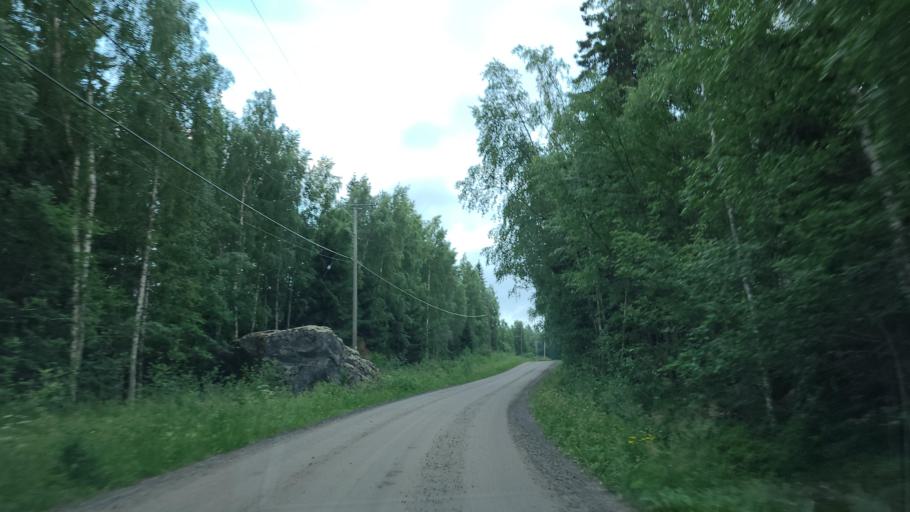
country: FI
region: Ostrobothnia
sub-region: Vaasa
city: Replot
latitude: 63.3088
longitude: 21.1579
